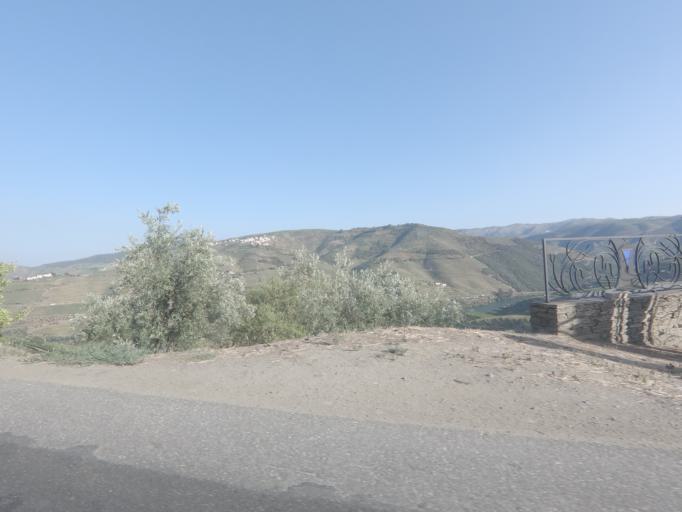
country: PT
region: Viseu
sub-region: Tabuaco
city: Tabuaco
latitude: 41.1741
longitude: -7.5725
